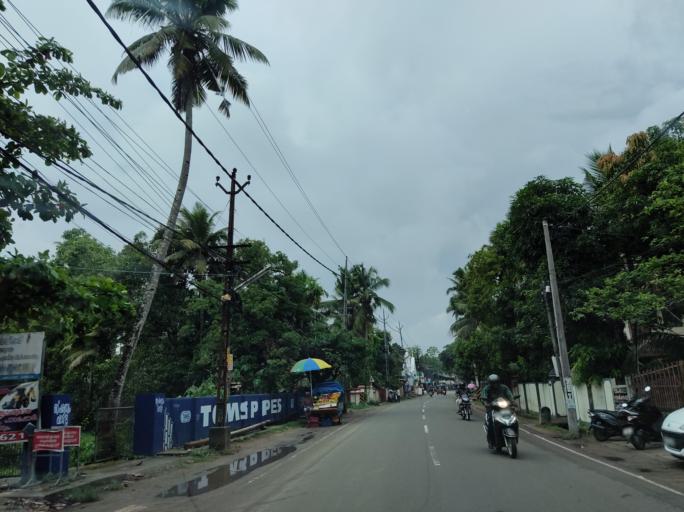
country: IN
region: Kerala
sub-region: Alappuzha
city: Mavelikara
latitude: 9.2430
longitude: 76.5198
